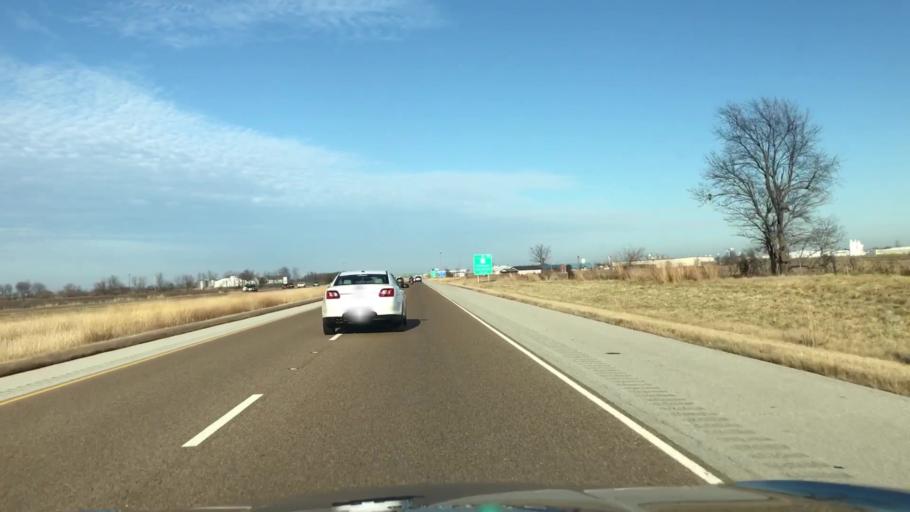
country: US
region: Illinois
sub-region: Montgomery County
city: Litchfield
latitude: 39.1661
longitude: -89.6893
